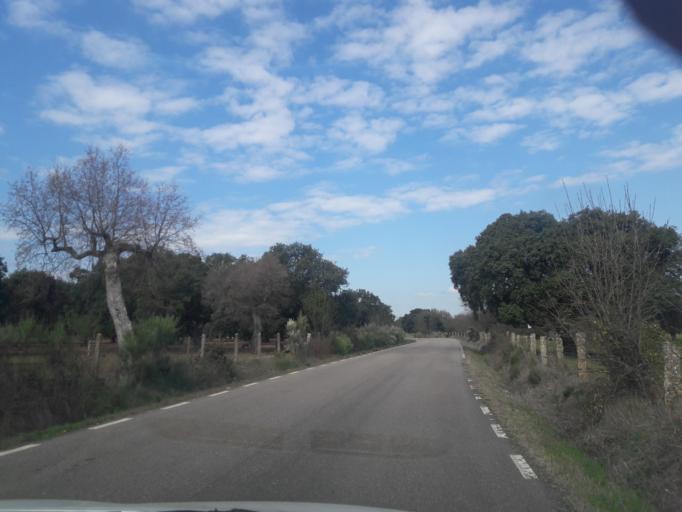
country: ES
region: Castille and Leon
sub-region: Provincia de Salamanca
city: Zamarra
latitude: 40.5544
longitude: -6.4468
